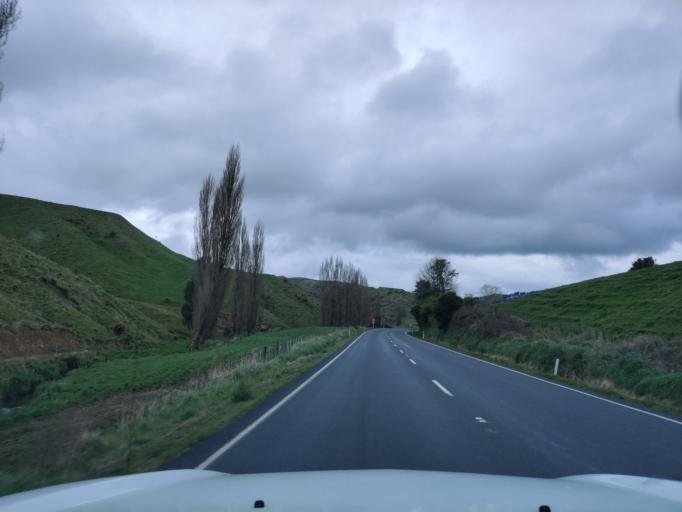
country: NZ
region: Waikato
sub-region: Otorohanga District
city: Otorohanga
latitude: -38.5195
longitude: 175.1905
